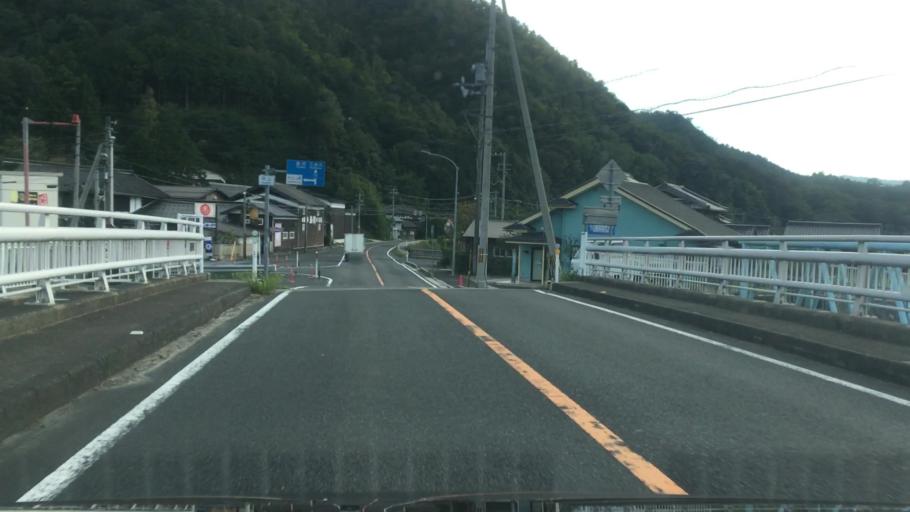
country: JP
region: Hyogo
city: Toyooka
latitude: 35.6085
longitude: 134.9190
